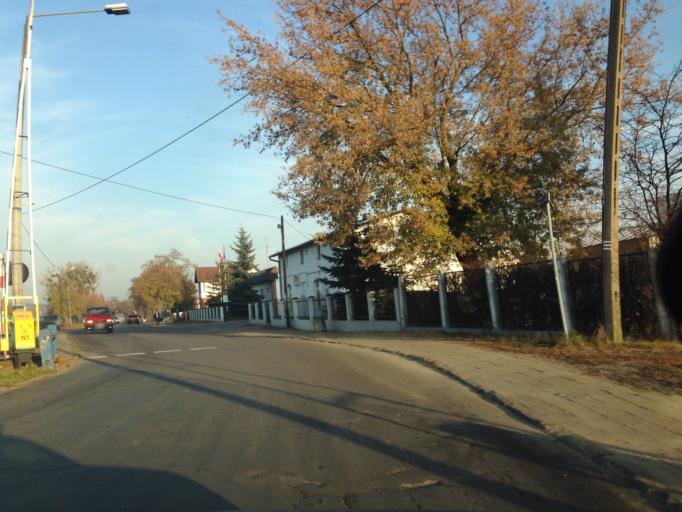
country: PL
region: Kujawsko-Pomorskie
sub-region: Powiat brodnicki
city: Brodnica
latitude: 53.2631
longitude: 19.3944
